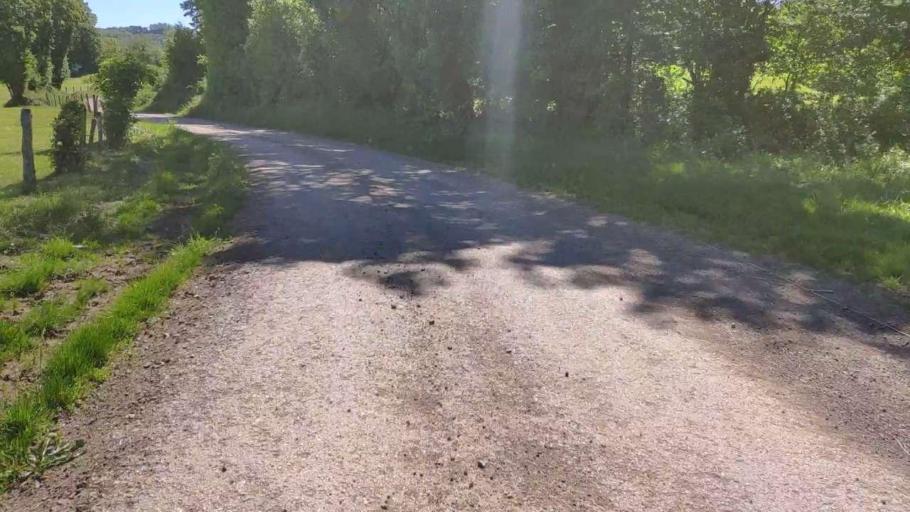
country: FR
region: Franche-Comte
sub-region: Departement du Jura
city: Clairvaux-les-Lacs
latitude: 46.6989
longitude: 5.7170
